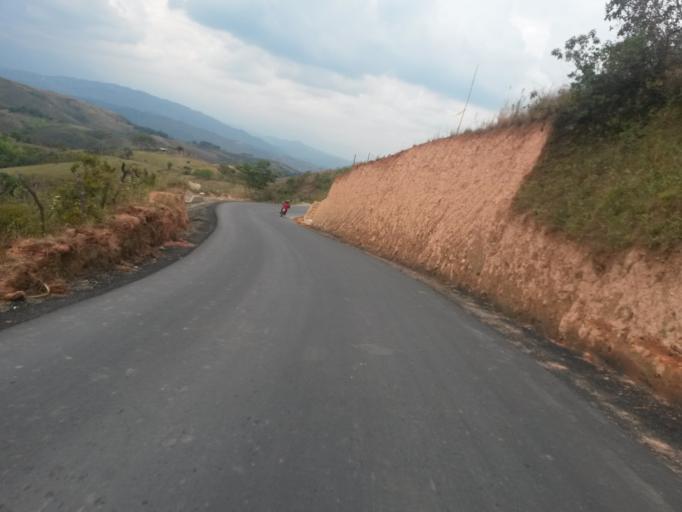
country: CO
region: Cauca
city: Buenos Aires
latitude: 3.0540
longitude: -76.6308
